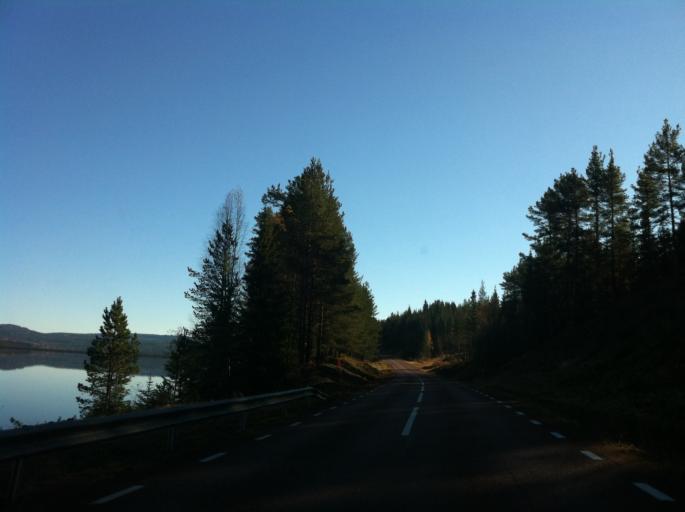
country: SE
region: Dalarna
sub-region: Alvdalens Kommun
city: AElvdalen
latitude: 61.3090
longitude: 13.7105
